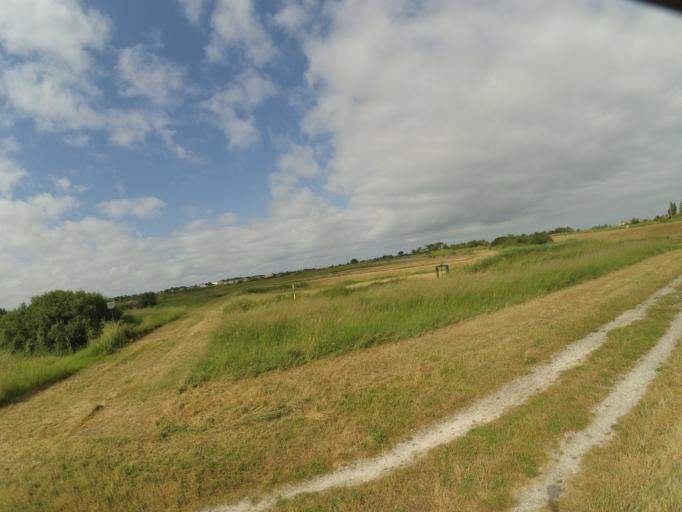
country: FR
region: Poitou-Charentes
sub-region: Departement de la Charente-Maritime
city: Angoulins
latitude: 46.1108
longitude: -1.1210
